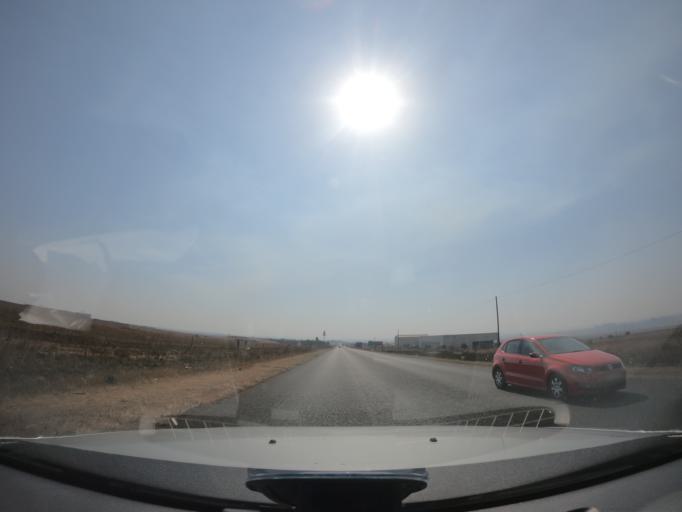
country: ZA
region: Mpumalanga
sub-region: Nkangala District Municipality
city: Middelburg
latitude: -25.8217
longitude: 29.4611
